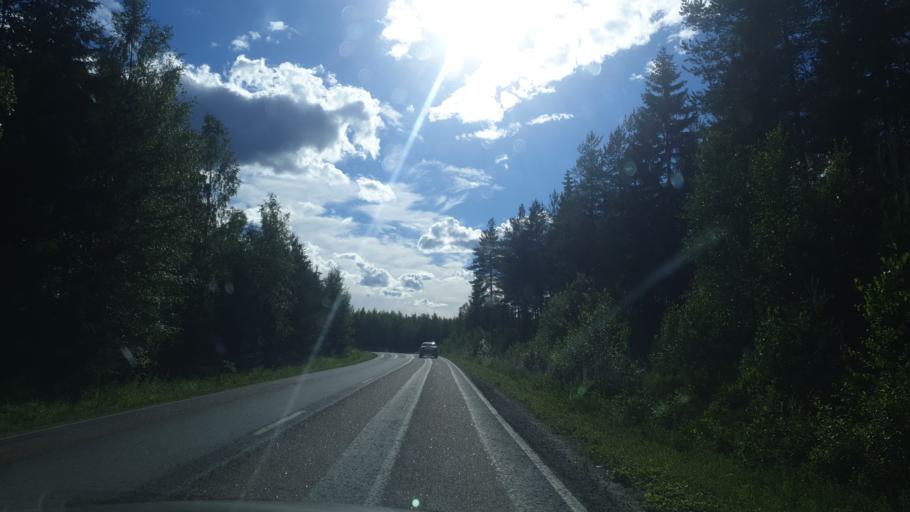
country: FI
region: Southern Savonia
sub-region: Mikkeli
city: Pertunmaa
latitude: 61.5220
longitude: 26.5745
